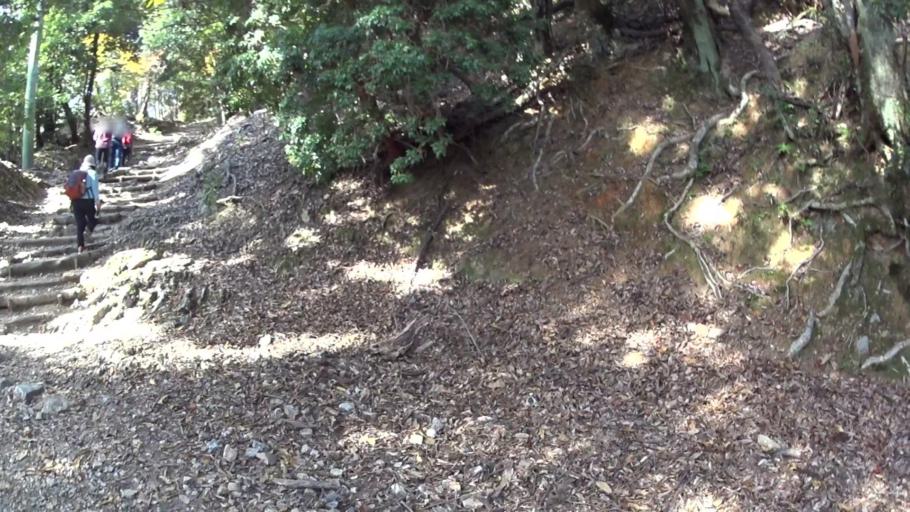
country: JP
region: Kyoto
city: Kameoka
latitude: 35.0422
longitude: 135.6525
